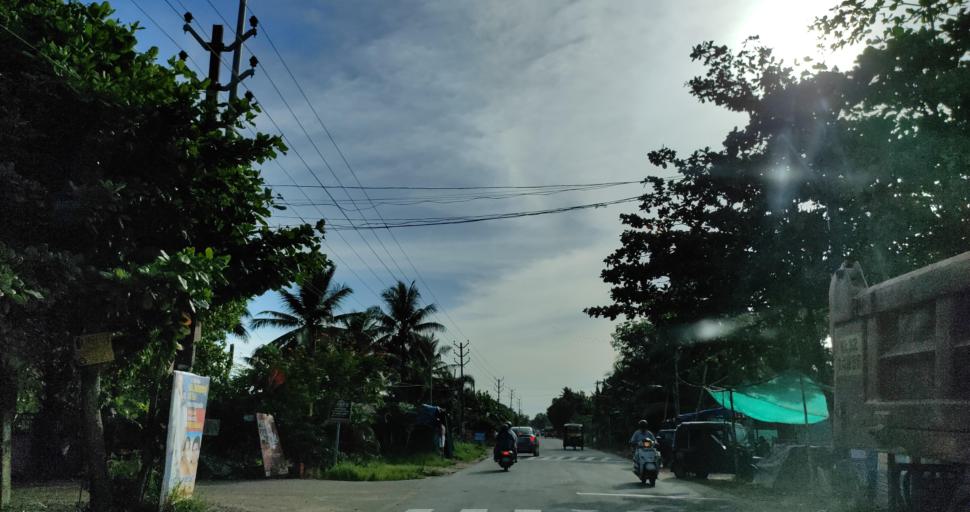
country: IN
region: Kerala
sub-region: Kottayam
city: Kottayam
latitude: 9.5923
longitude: 76.4487
